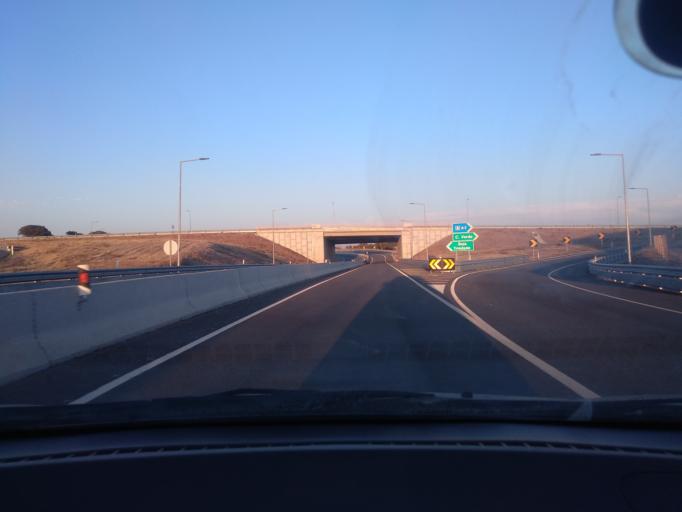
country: PT
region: Beja
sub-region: Beja
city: Beja
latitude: 37.8644
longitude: -7.9538
